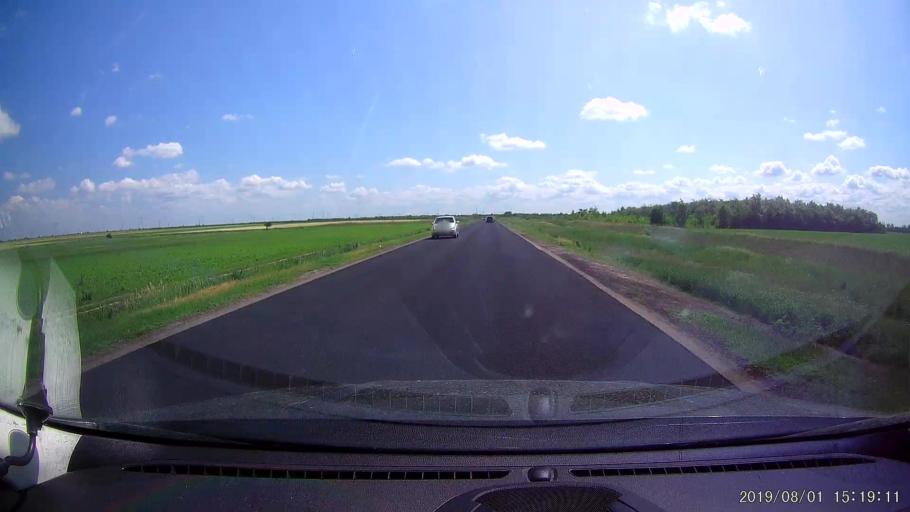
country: RO
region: Braila
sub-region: Comuna Unirea
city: Unirea
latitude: 45.0934
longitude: 27.8146
